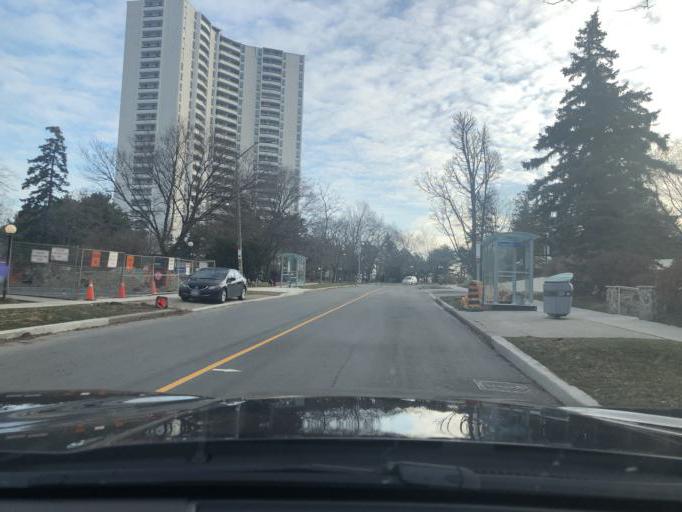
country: CA
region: Ontario
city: Willowdale
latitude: 43.7646
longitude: -79.3445
